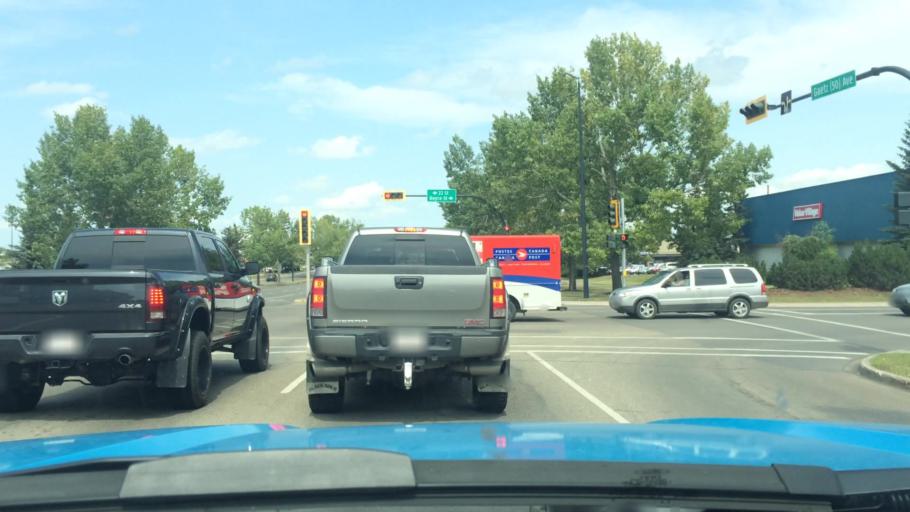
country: CA
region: Alberta
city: Red Deer
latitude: 52.2386
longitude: -113.8139
